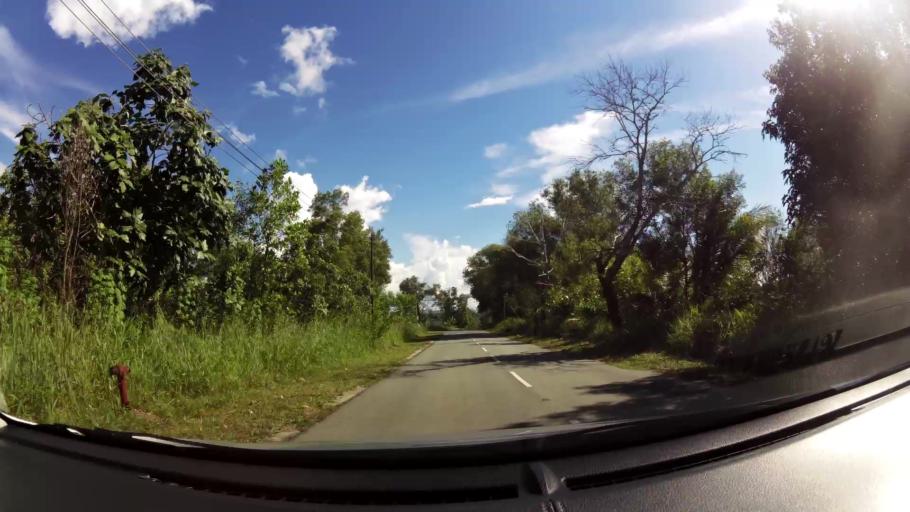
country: BN
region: Brunei and Muara
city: Bandar Seri Begawan
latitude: 4.9673
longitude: 114.9346
